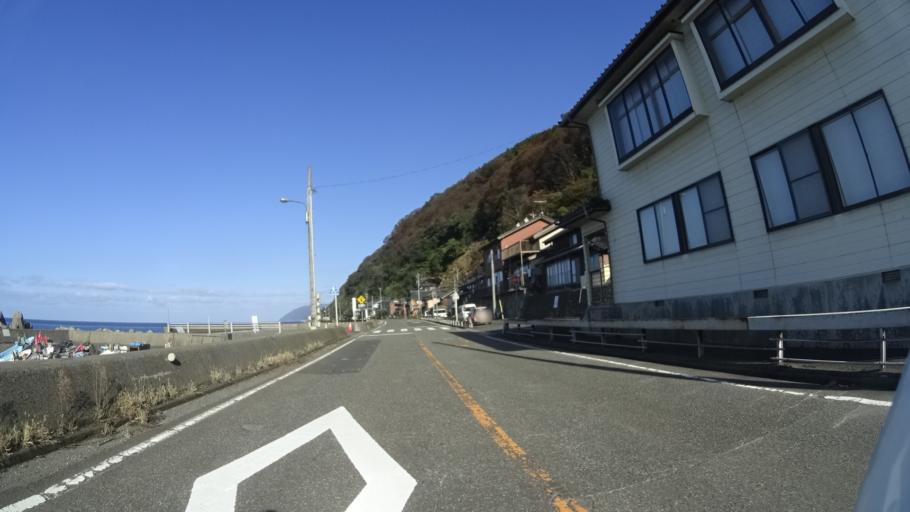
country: JP
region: Fukui
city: Takefu
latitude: 35.7815
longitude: 136.0982
